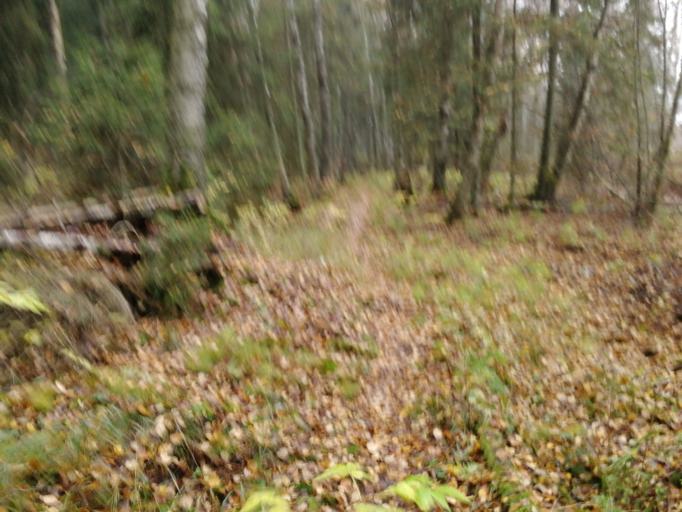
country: FI
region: Pirkanmaa
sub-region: Tampere
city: Tampere
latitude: 61.4487
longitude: 23.8910
